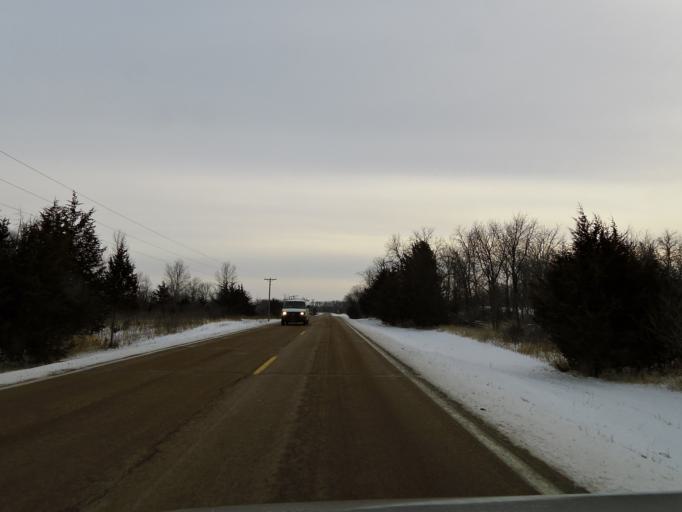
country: US
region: Minnesota
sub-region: Hennepin County
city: Saint Bonifacius
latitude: 44.8865
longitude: -93.7043
